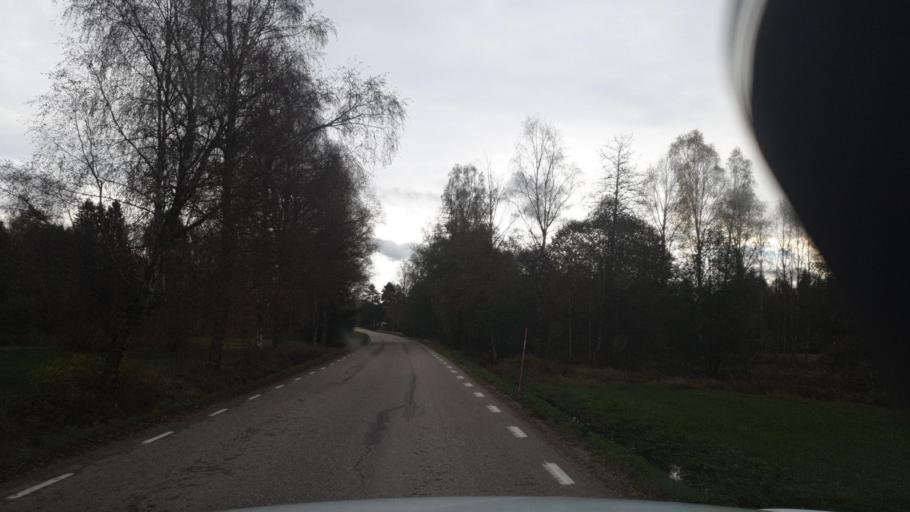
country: SE
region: Vaermland
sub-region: Arvika Kommun
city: Arvika
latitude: 59.7475
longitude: 12.8037
